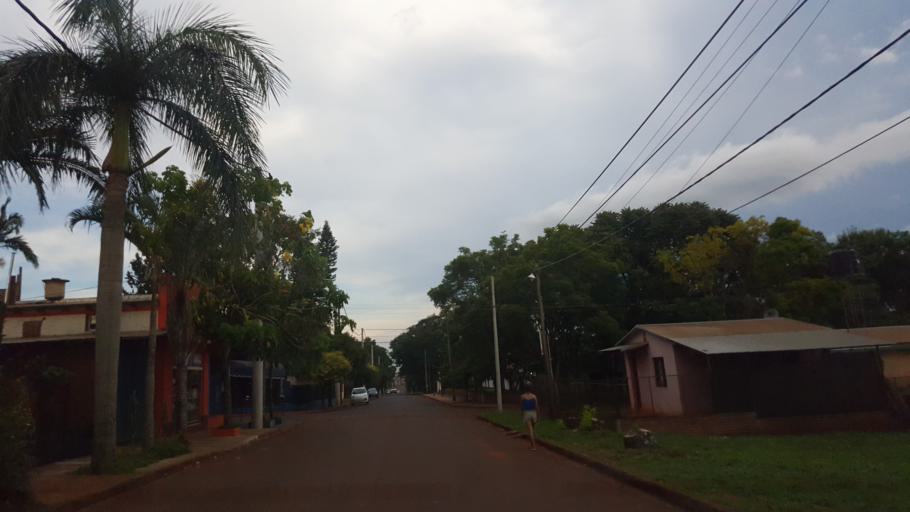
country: AR
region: Misiones
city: Jardin America
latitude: -27.0481
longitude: -55.2414
